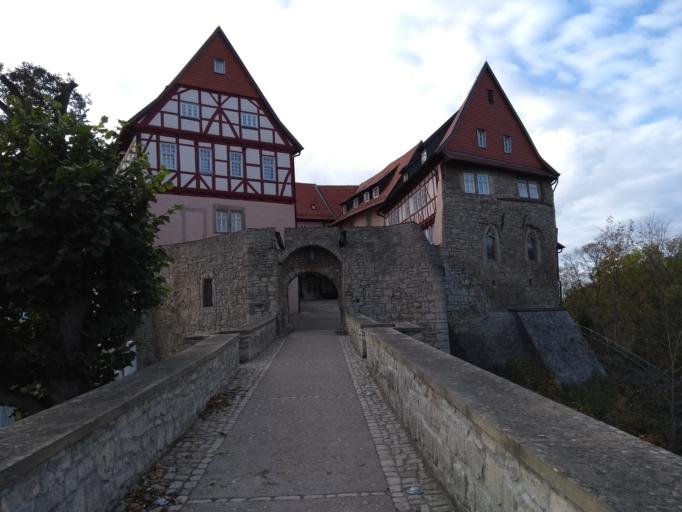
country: DE
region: Thuringia
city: Tastungen
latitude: 51.4534
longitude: 10.3432
